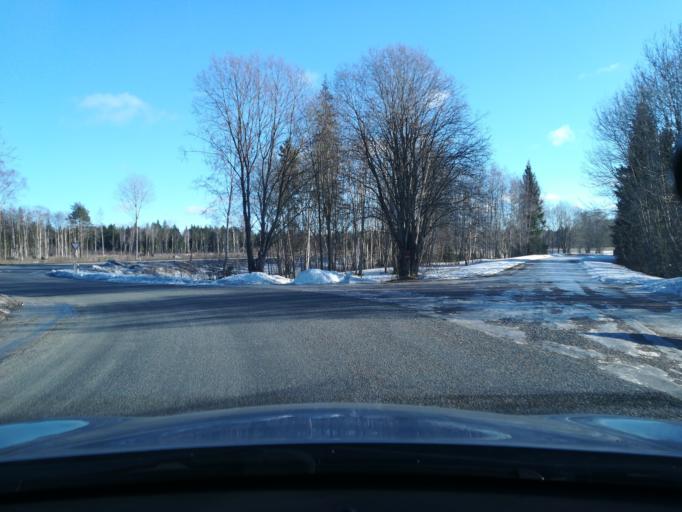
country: EE
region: Raplamaa
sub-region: Kohila vald
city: Kohila
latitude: 59.2322
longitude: 24.7710
